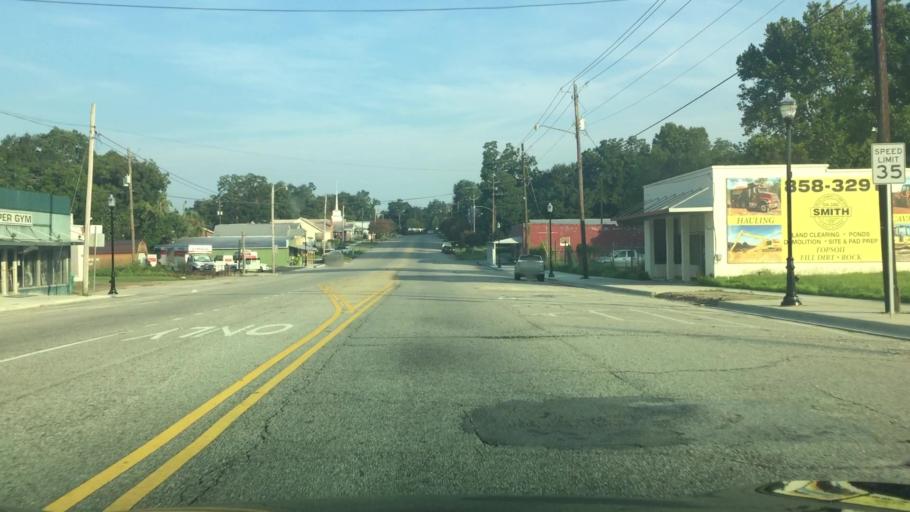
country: US
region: Alabama
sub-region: Covington County
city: Florala
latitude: 31.0068
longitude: -86.3301
